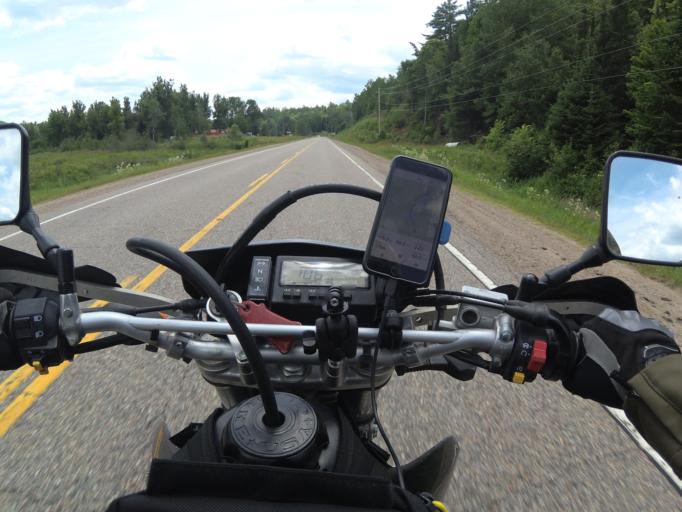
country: CA
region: Ontario
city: Bancroft
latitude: 45.0117
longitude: -77.2761
